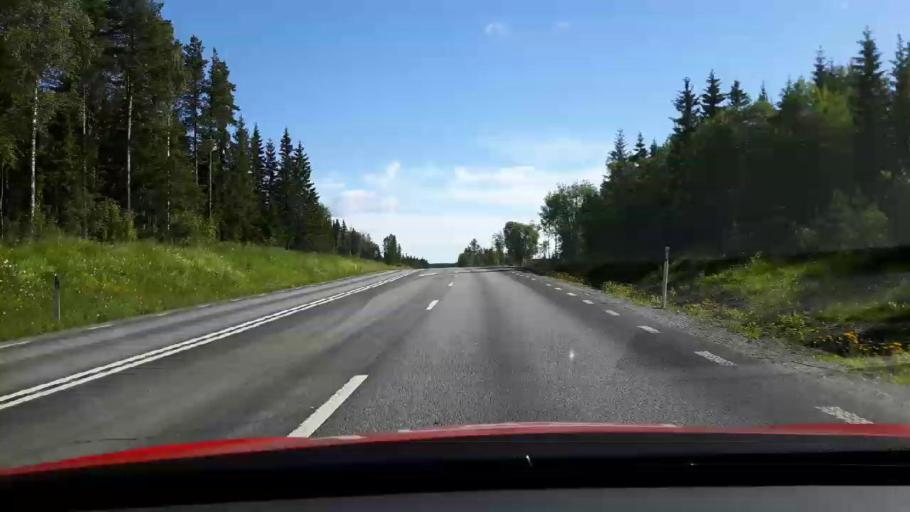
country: SE
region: Jaemtland
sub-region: OEstersunds Kommun
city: Ostersund
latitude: 63.2151
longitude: 14.7263
